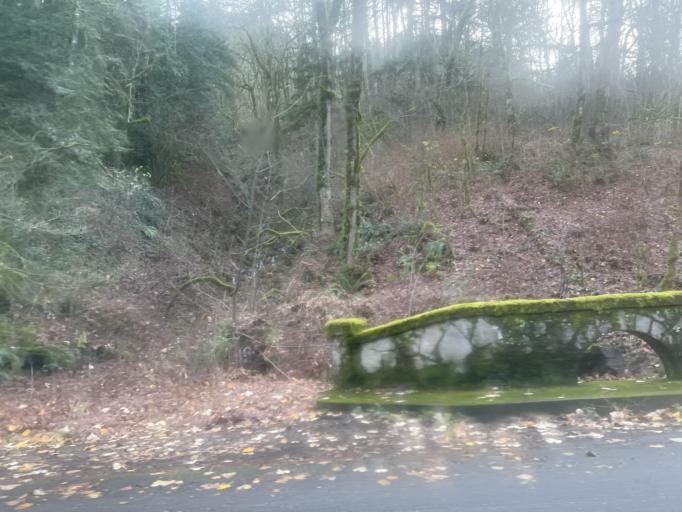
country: US
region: Washington
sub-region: Clark County
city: Washougal
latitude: 45.5392
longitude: -122.2169
